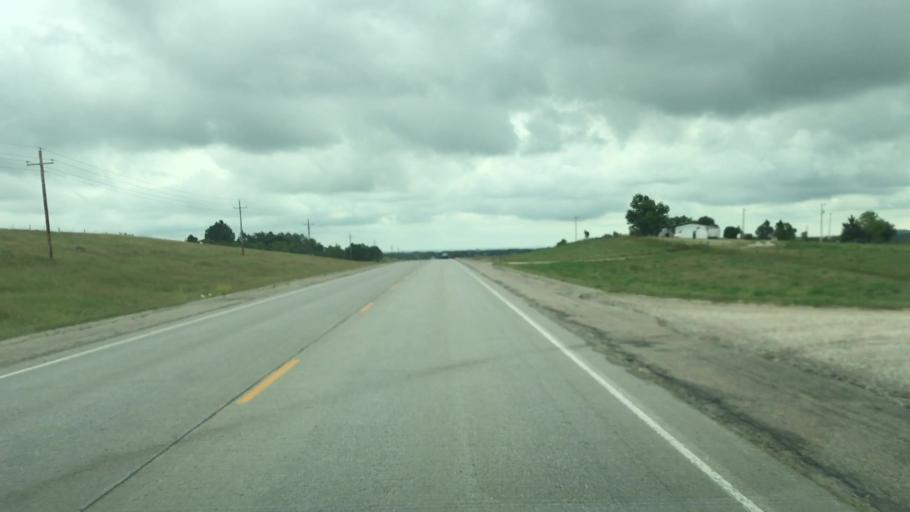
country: US
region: South Dakota
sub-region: Todd County
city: Mission
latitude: 43.3029
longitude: -100.6966
